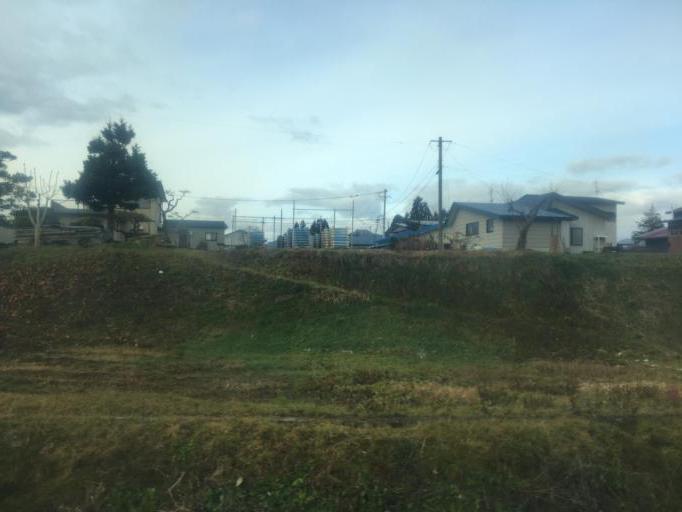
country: JP
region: Akita
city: Odate
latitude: 40.3015
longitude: 140.5682
